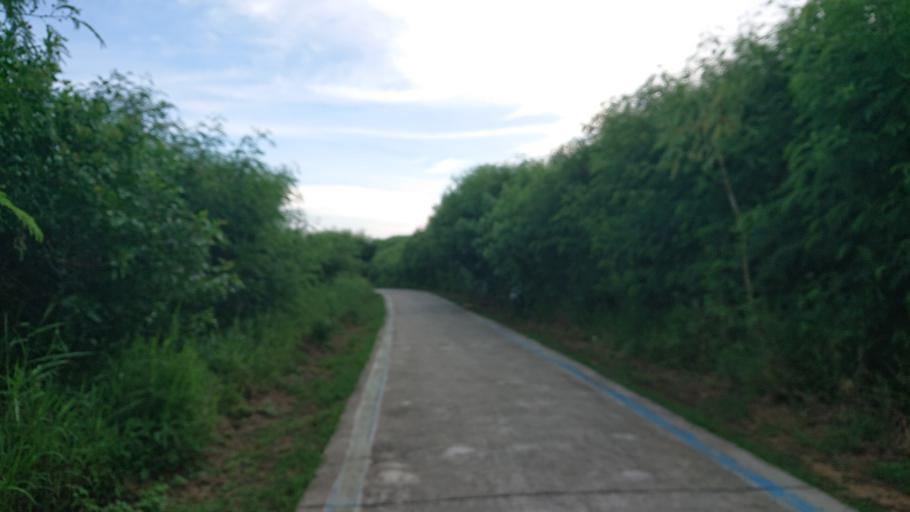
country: TW
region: Taiwan
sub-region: Penghu
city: Ma-kung
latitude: 23.5173
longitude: 119.6060
